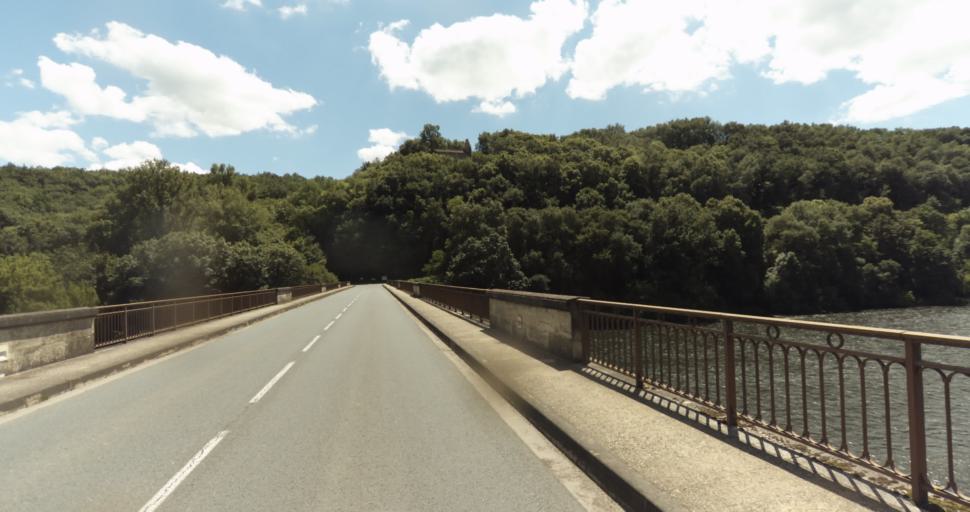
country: FR
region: Aquitaine
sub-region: Departement de la Dordogne
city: Lalinde
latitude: 44.8348
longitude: 0.7402
